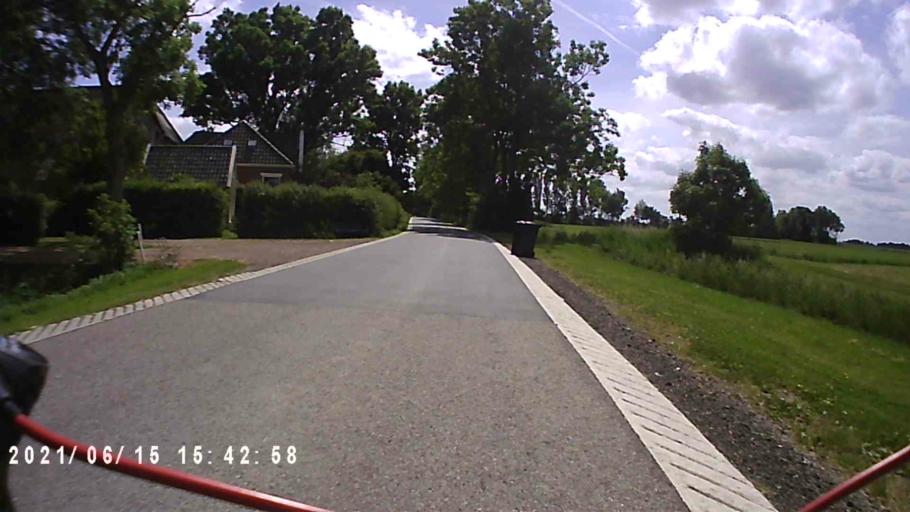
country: NL
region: Groningen
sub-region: Gemeente Bedum
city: Bedum
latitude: 53.2807
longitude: 6.5671
